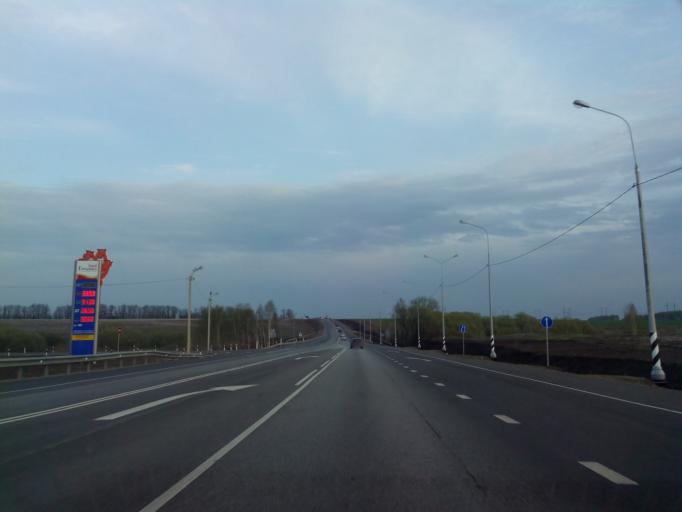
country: RU
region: Rjazan
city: Ryazhsk
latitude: 53.5570
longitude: 40.0532
